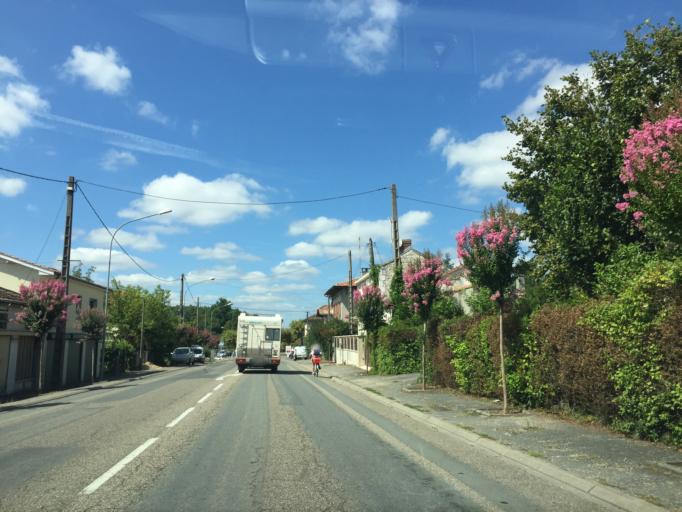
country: FR
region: Aquitaine
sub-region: Departement du Lot-et-Garonne
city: Casteljaloux
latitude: 44.3112
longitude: 0.0926
